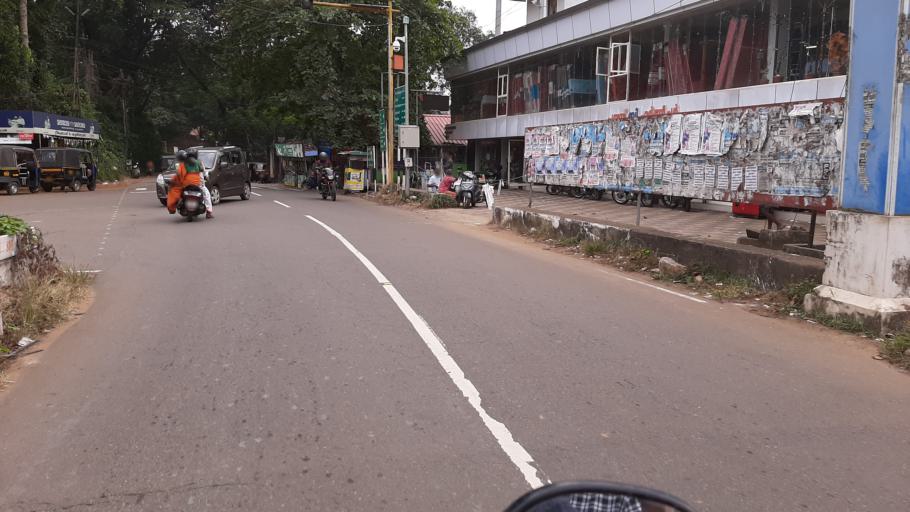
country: IN
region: Kerala
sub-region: Kottayam
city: Erattupetta
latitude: 9.4952
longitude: 76.8492
